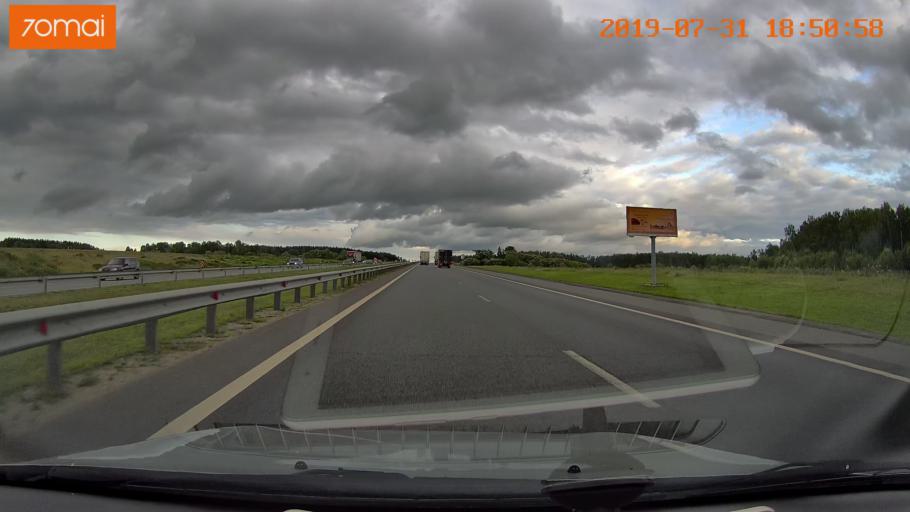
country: RU
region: Moskovskaya
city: Troitskoye
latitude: 55.2251
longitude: 38.5953
